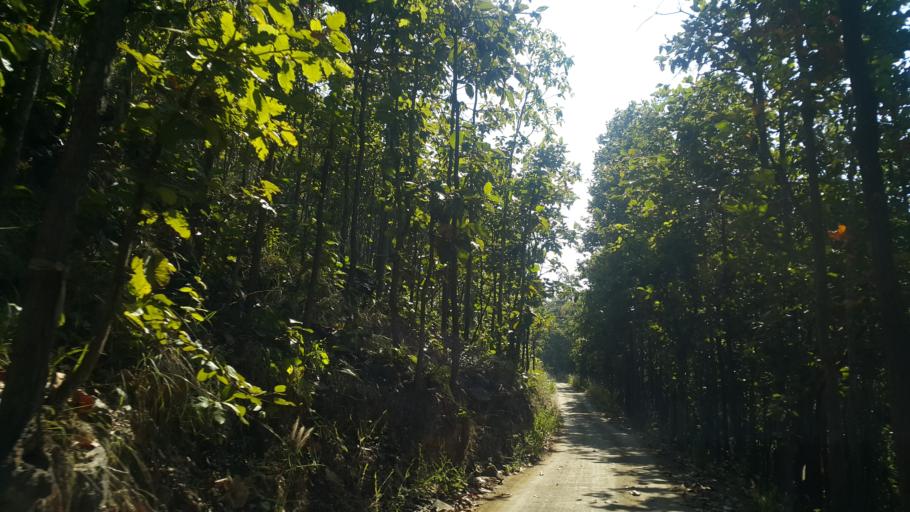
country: TH
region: Lamphun
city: Ban Thi
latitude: 18.6687
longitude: 99.1831
